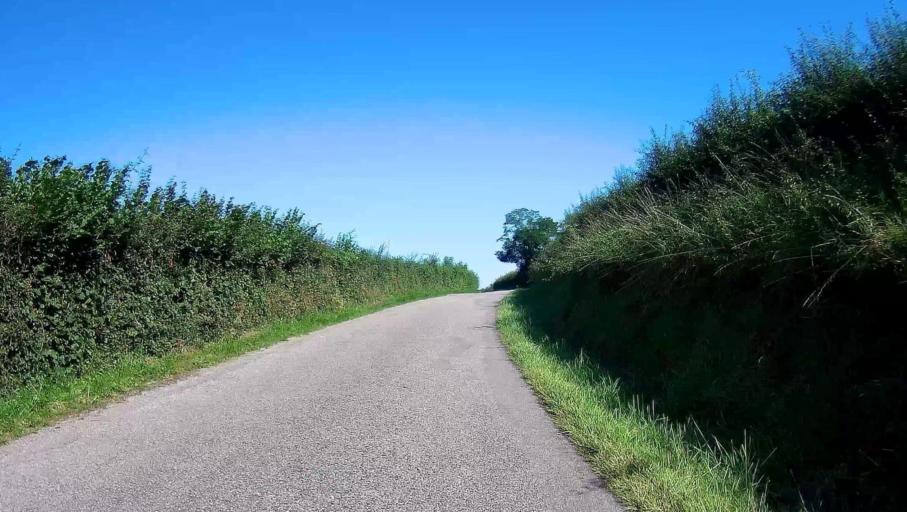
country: FR
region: Bourgogne
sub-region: Departement de Saone-et-Loire
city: Saint-Leger-sur-Dheune
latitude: 46.8276
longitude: 4.5944
